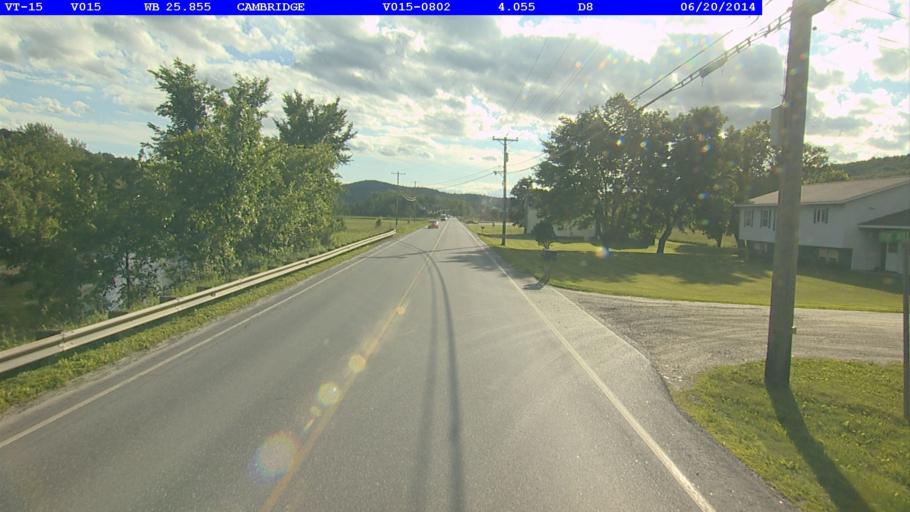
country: US
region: Vermont
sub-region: Lamoille County
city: Johnson
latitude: 44.6457
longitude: -72.8487
